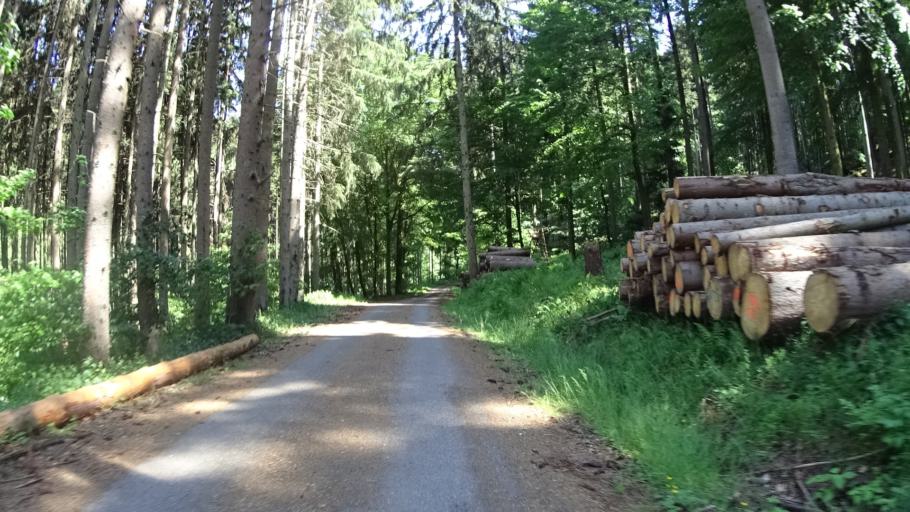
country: DE
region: Baden-Wuerttemberg
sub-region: Karlsruhe Region
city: Hopfingen
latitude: 49.6308
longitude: 9.4414
